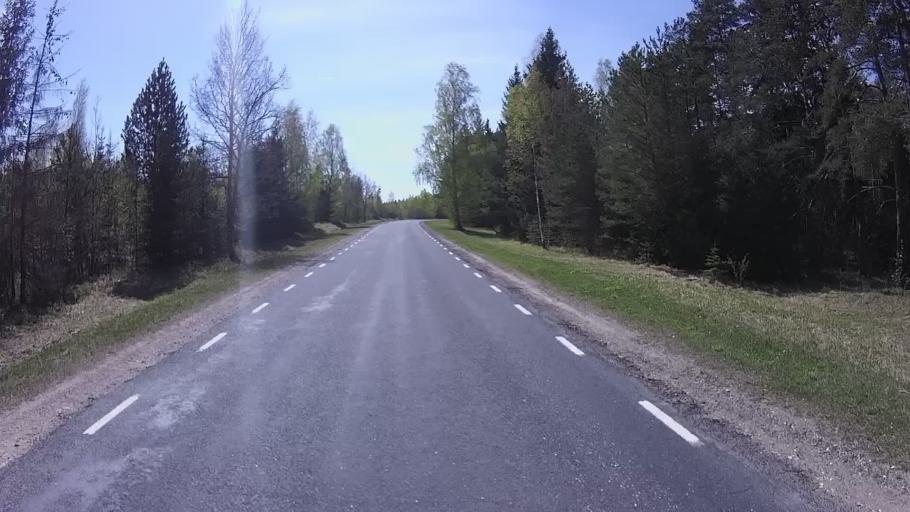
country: EE
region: Laeaene
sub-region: Ridala Parish
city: Uuemoisa
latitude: 59.0382
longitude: 23.8288
